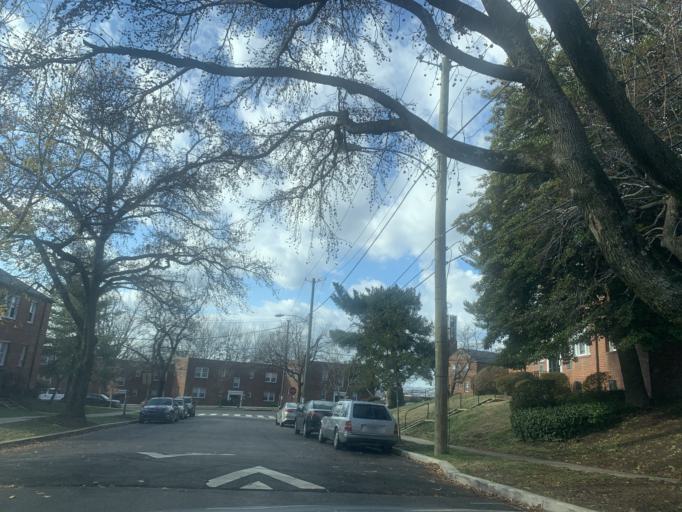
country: US
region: Maryland
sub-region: Prince George's County
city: Coral Hills
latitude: 38.8848
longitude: -76.9501
